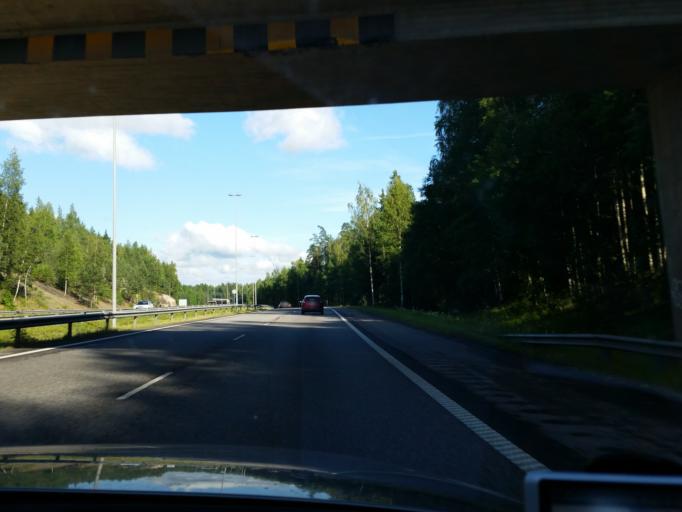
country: FI
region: Uusimaa
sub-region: Helsinki
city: Vihti
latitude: 60.2922
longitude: 24.3902
